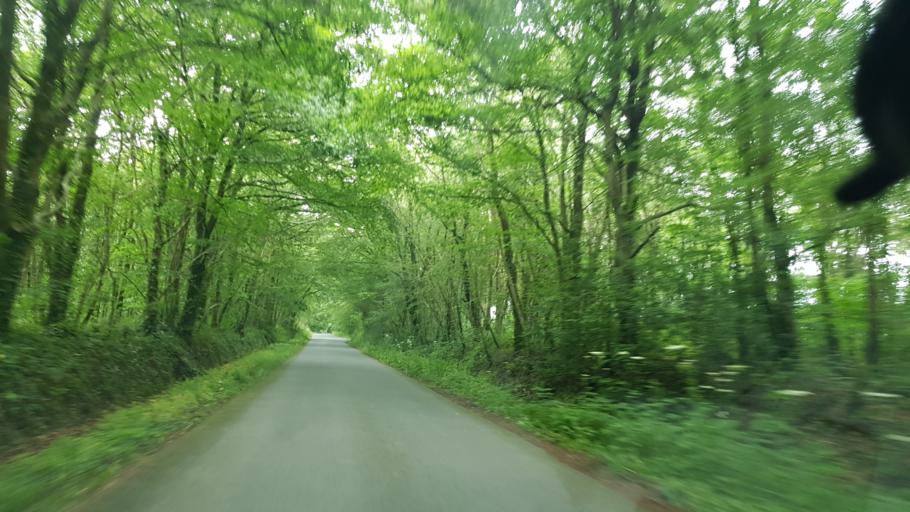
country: GB
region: Wales
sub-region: Pembrokeshire
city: Wiston
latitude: 51.7935
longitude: -4.8974
